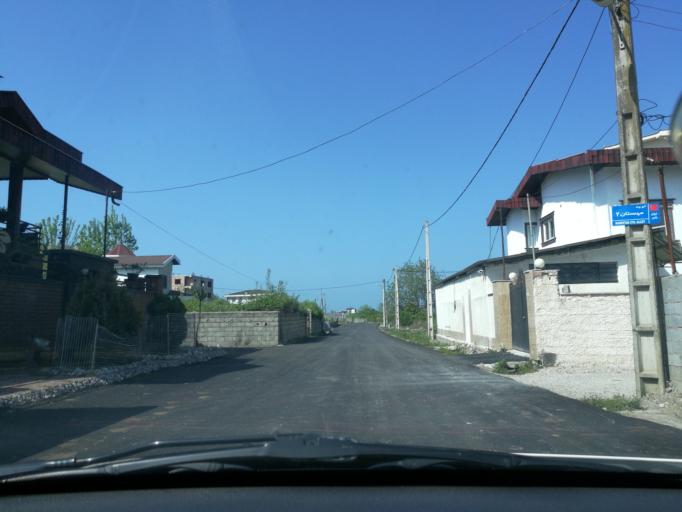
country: IR
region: Mazandaran
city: Chalus
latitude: 36.6701
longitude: 51.4324
